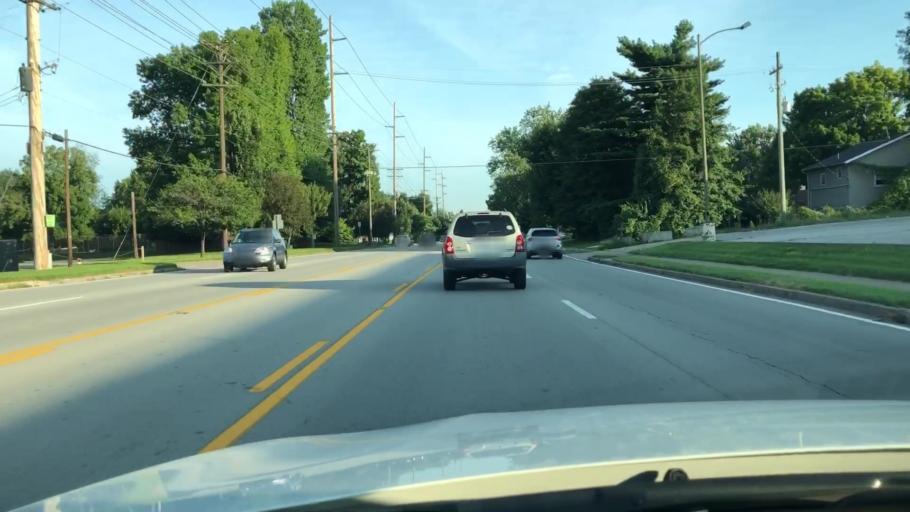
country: US
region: Kentucky
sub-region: Jefferson County
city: Saint Regis Park
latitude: 38.2216
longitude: -85.6320
